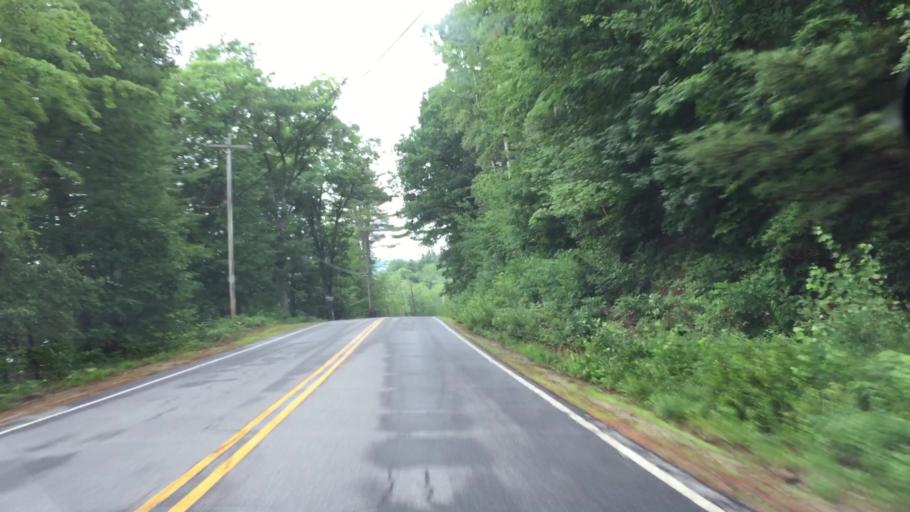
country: US
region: New Hampshire
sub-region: Carroll County
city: Center Harbor
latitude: 43.7505
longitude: -71.4807
